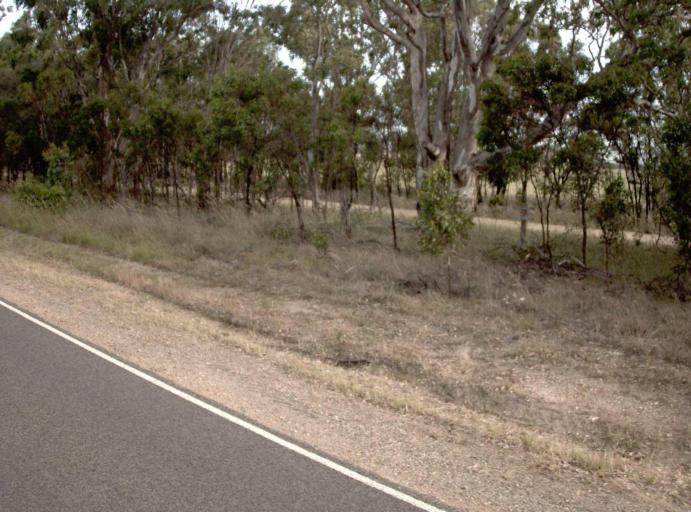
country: AU
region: Victoria
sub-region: Wellington
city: Heyfield
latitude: -37.9817
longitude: 146.8099
